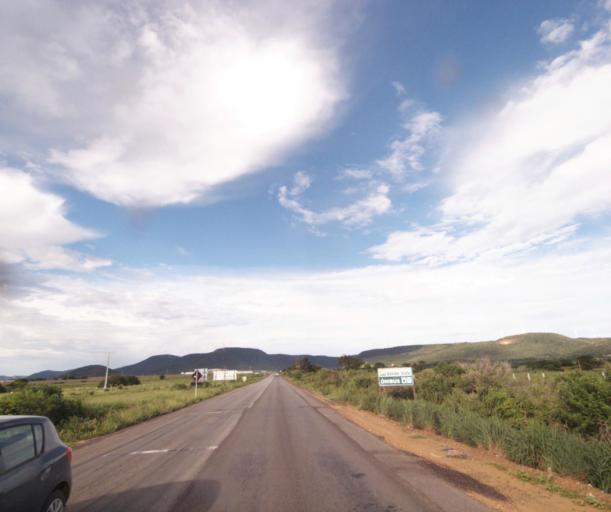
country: BR
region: Bahia
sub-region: Guanambi
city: Guanambi
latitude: -14.1813
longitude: -42.7349
